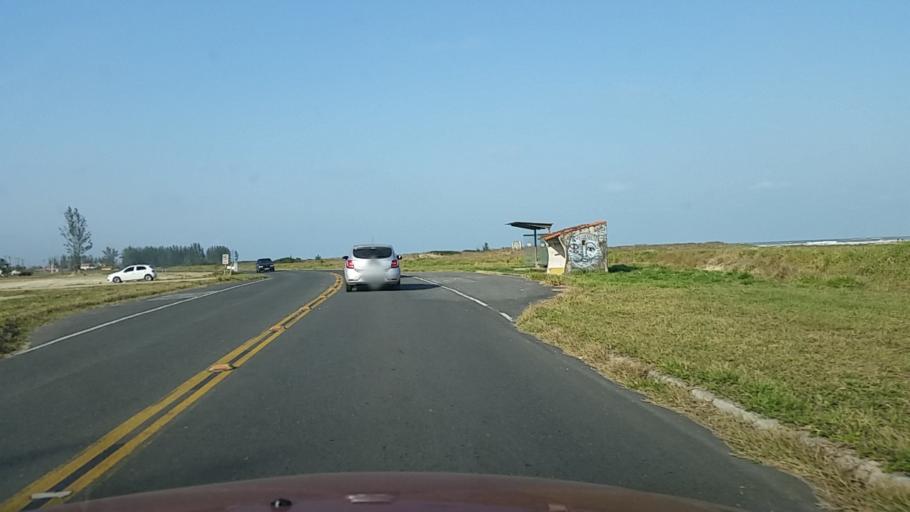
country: BR
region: Sao Paulo
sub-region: Iguape
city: Iguape
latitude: -24.8037
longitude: -47.6341
